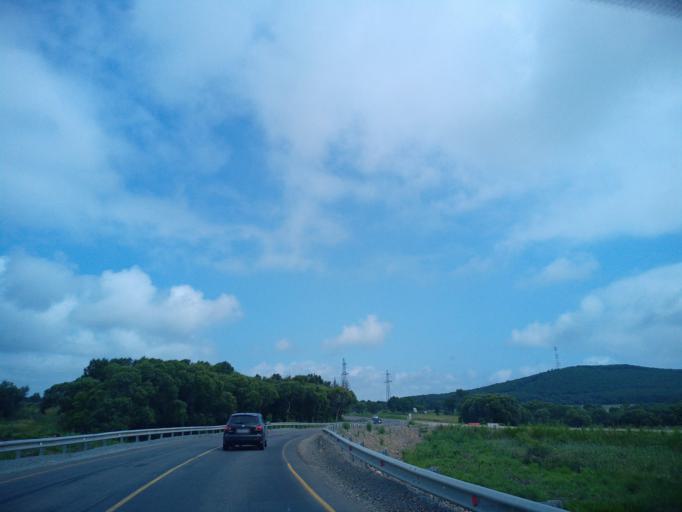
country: RU
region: Primorskiy
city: Dal'nerechensk
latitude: 46.0671
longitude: 133.8951
